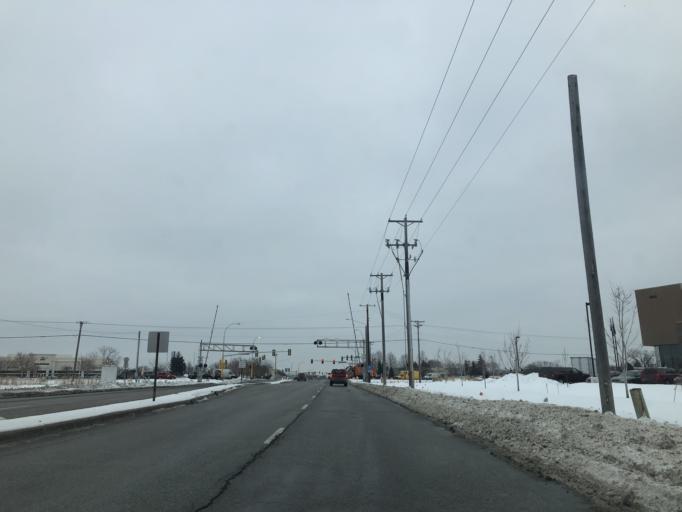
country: US
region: Minnesota
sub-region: Hennepin County
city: Osseo
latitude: 45.0945
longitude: -93.3862
